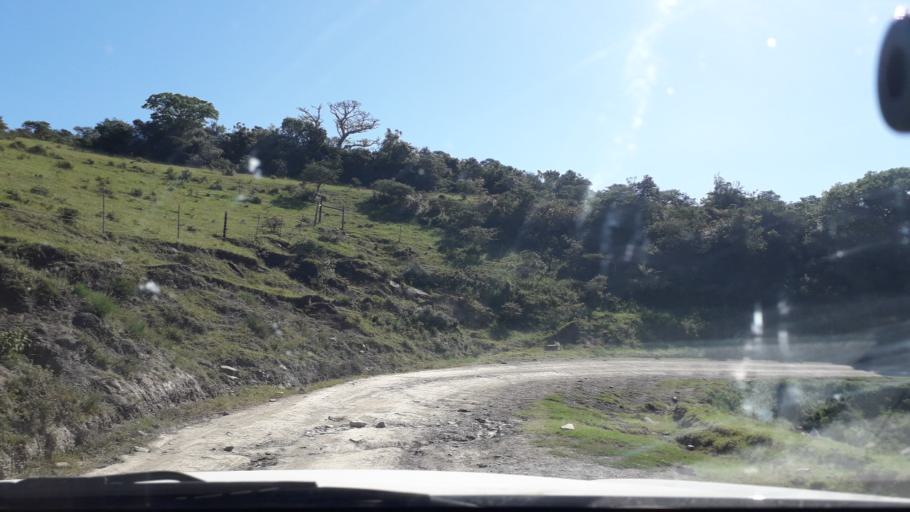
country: ZA
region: Eastern Cape
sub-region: Amathole District Municipality
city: Komga
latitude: -32.7885
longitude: 27.9523
